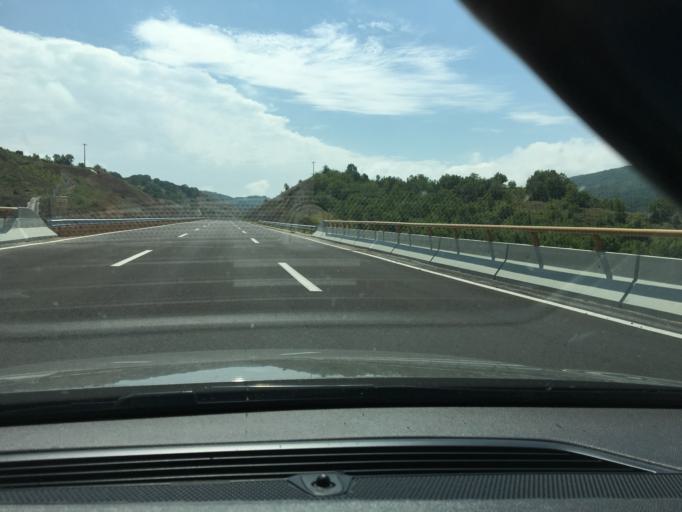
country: MK
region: Petrovec
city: Sredno Konjare
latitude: 41.9490
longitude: 21.7722
